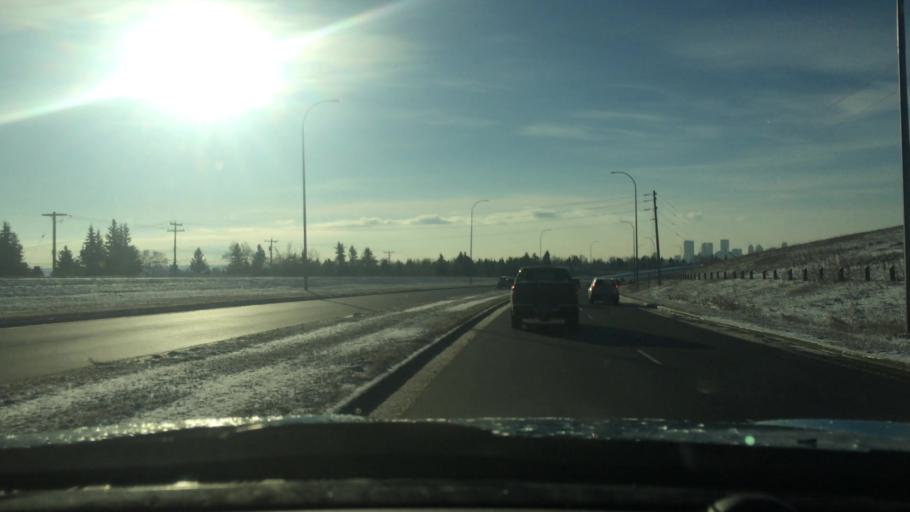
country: CA
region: Alberta
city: Calgary
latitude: 51.1150
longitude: -114.0844
